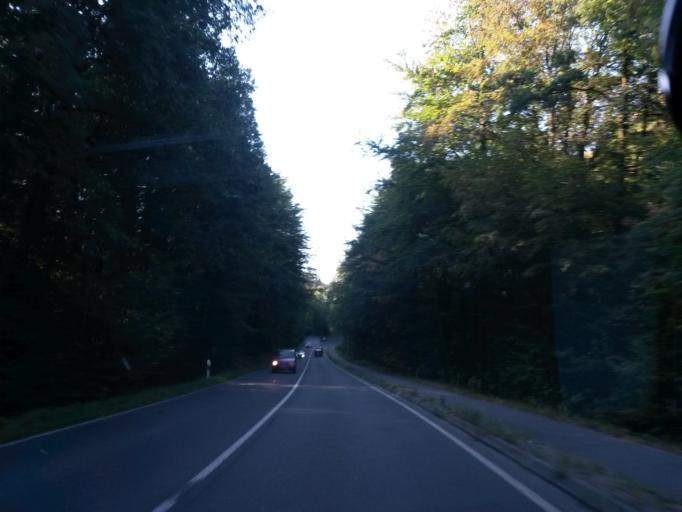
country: DE
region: North Rhine-Westphalia
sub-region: Regierungsbezirk Koln
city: Bergisch Gladbach
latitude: 50.9507
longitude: 7.1687
